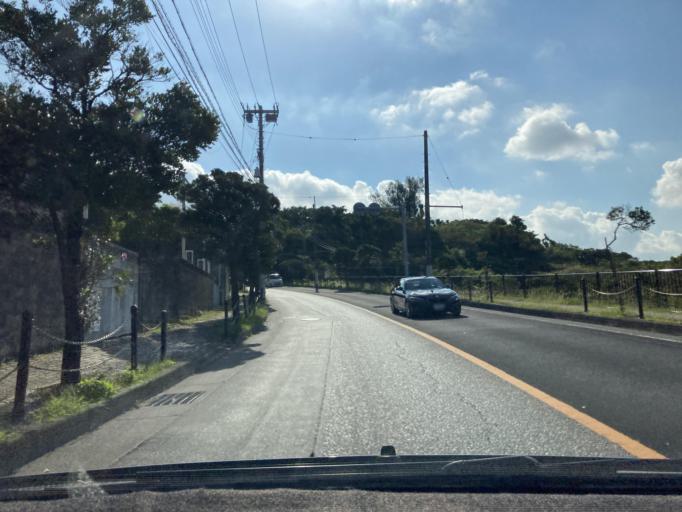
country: JP
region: Okinawa
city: Naha-shi
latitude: 26.2097
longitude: 127.7202
